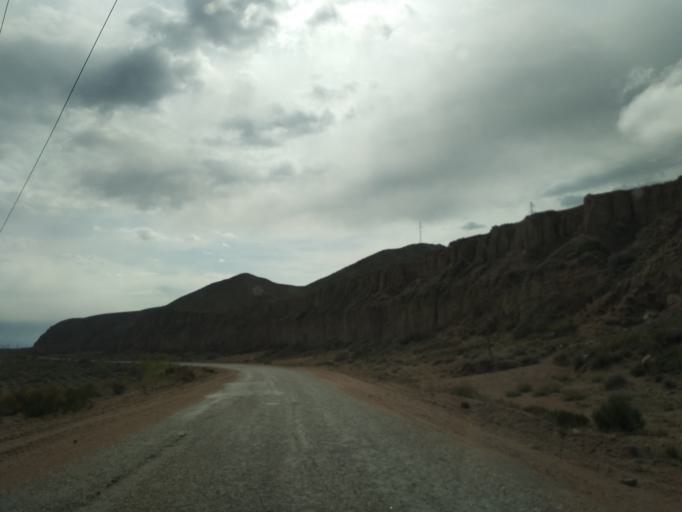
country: KG
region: Ysyk-Koel
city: Kadzhi-Say
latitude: 42.1786
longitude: 77.2963
